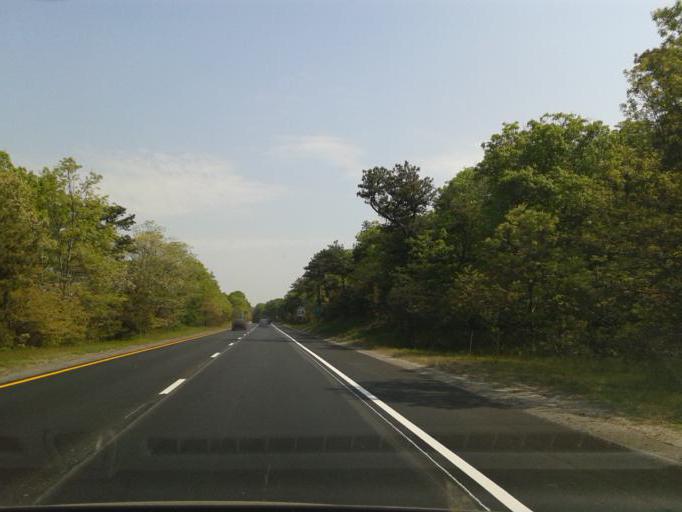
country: US
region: Massachusetts
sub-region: Barnstable County
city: Pocasset
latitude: 41.6929
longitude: -70.5878
